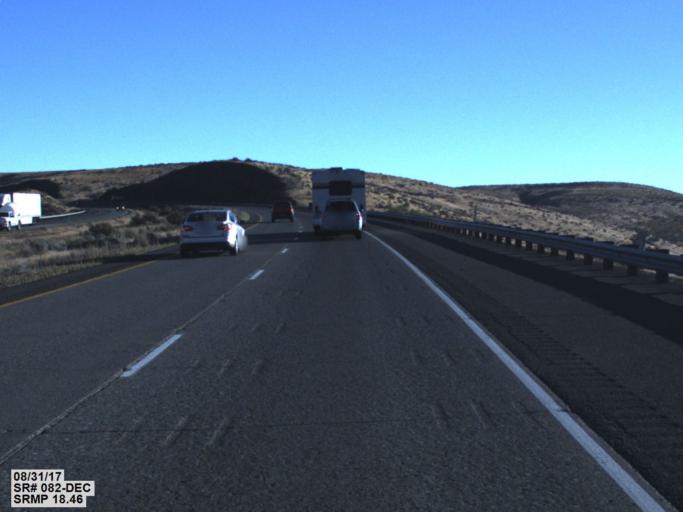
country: US
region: Washington
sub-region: Yakima County
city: Terrace Heights
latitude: 46.7562
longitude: -120.3828
